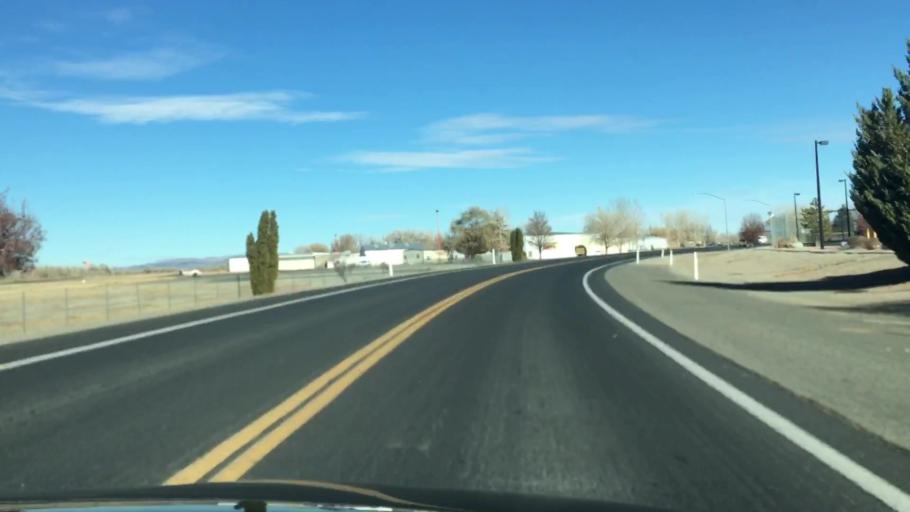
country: US
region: Nevada
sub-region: Lyon County
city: Yerington
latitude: 38.9964
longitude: -119.1618
